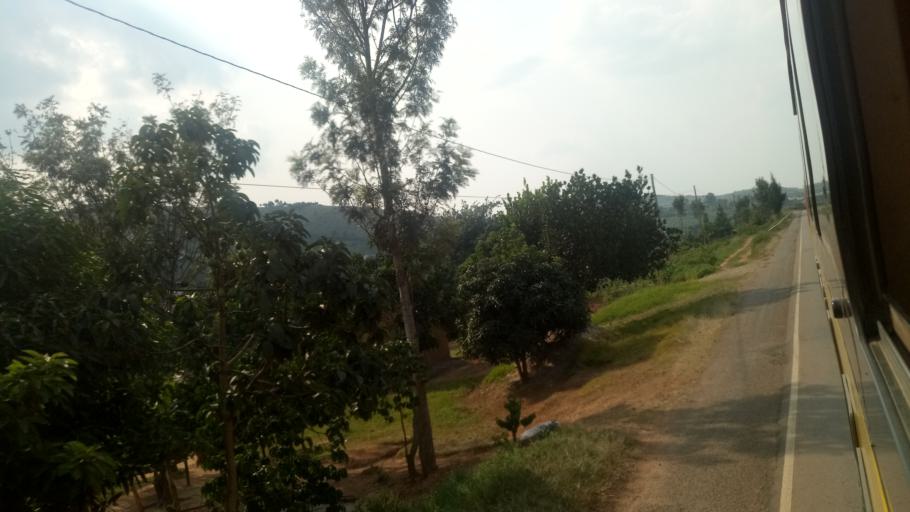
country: UG
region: Western Region
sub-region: Mbarara District
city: Mbarara
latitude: -0.5394
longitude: 30.7146
